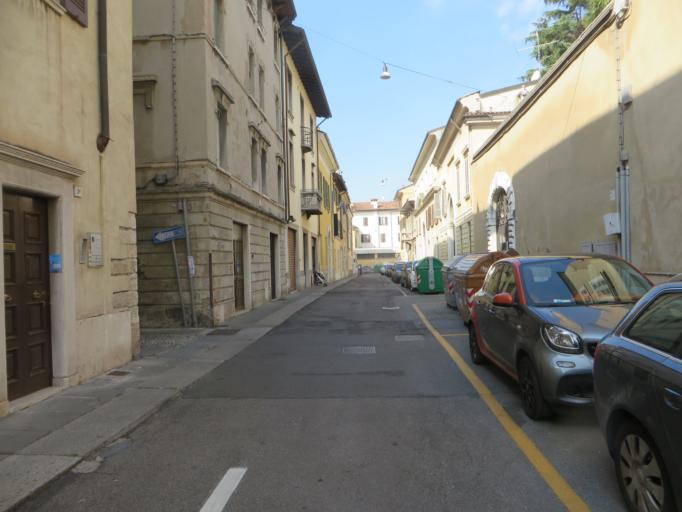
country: IT
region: Lombardy
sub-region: Provincia di Brescia
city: Brescia
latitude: 45.5387
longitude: 10.2134
